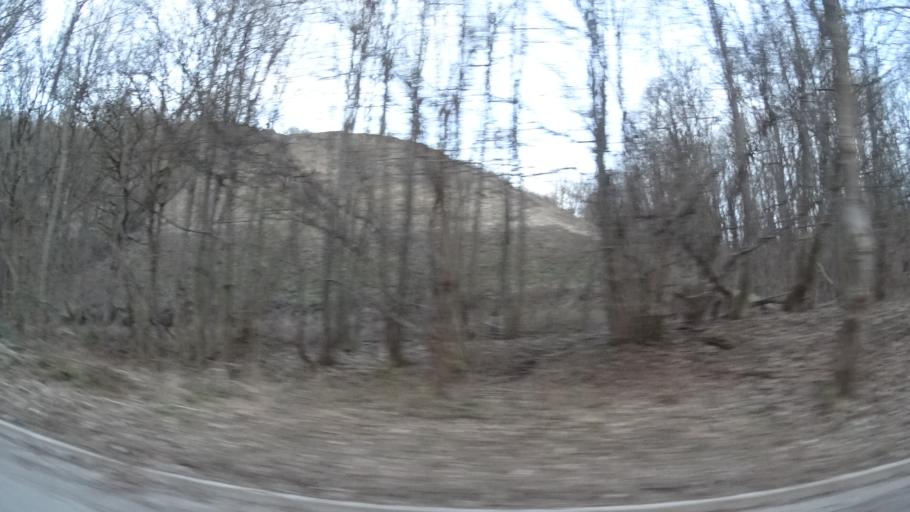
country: DE
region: Baden-Wuerttemberg
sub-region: Regierungsbezirk Stuttgart
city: Markgroningen
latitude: 48.9097
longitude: 9.0665
